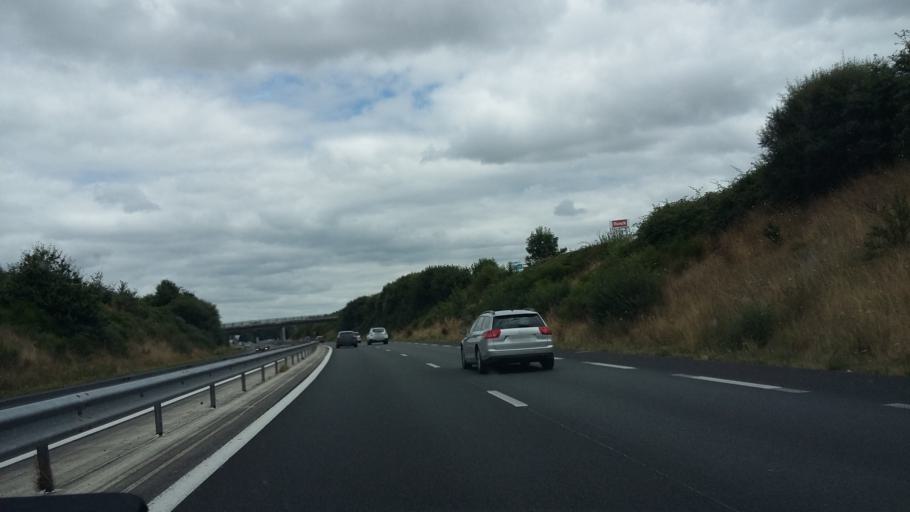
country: FR
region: Pays de la Loire
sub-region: Departement de la Vendee
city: Aizenay
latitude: 46.7316
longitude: -1.6025
